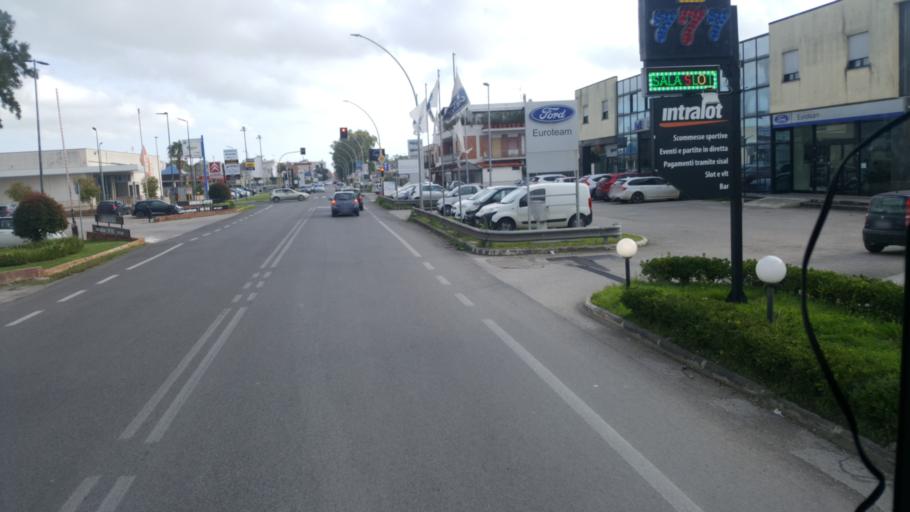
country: IT
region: Latium
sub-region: Provincia di Latina
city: Latina
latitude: 41.4757
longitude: 12.8806
